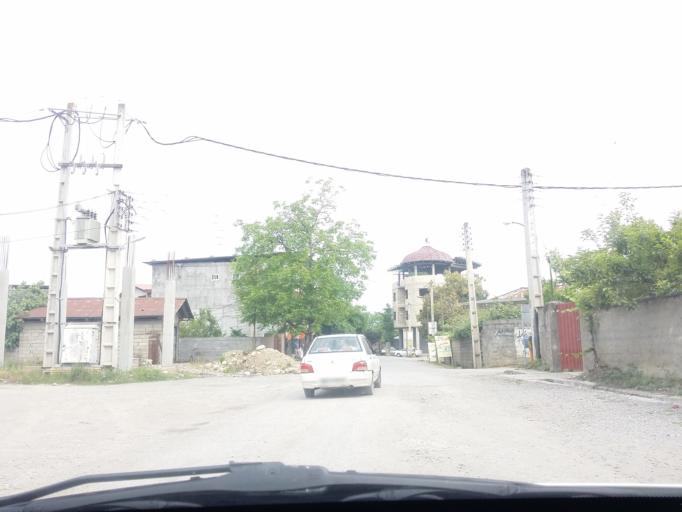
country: IR
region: Mazandaran
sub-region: Nowshahr
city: Nowshahr
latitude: 36.6234
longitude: 51.4935
